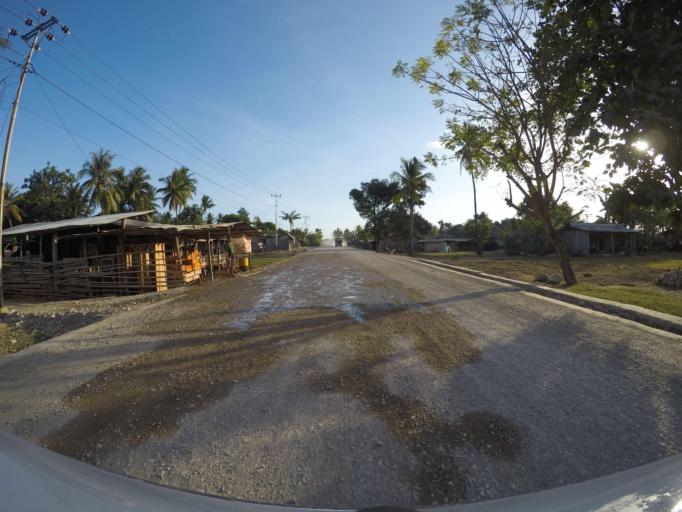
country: TL
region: Viqueque
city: Viqueque
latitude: -8.8259
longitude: 126.5286
